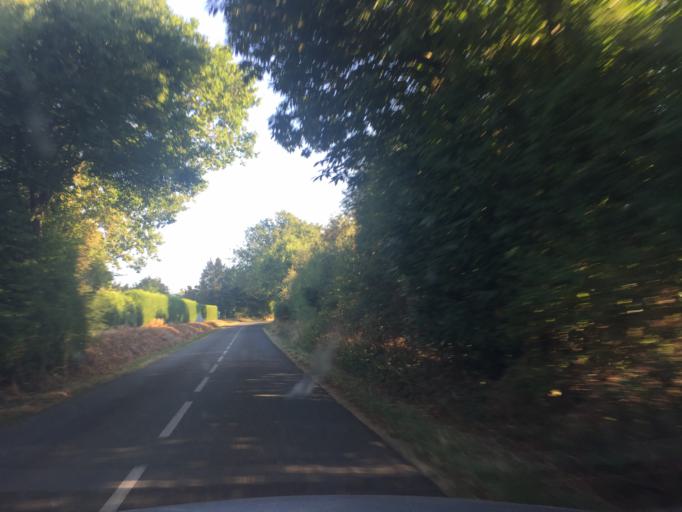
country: FR
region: Poitou-Charentes
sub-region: Departement des Deux-Sevres
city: Lezay
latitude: 46.1939
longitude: -0.0382
